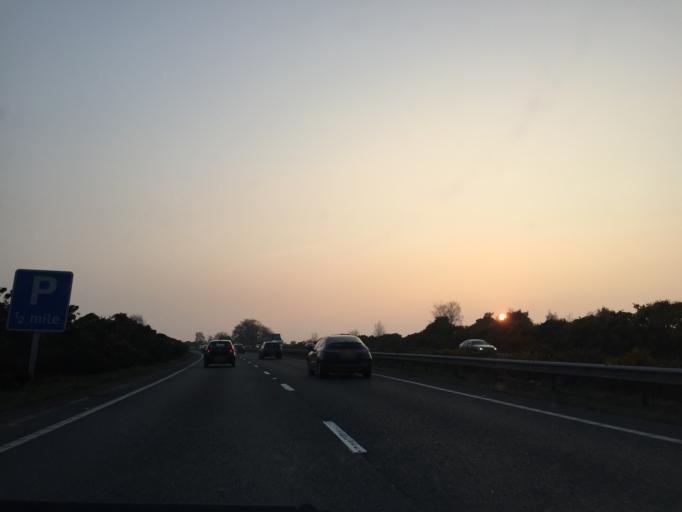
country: GB
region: England
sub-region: Hampshire
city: Cadnam
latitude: 50.8966
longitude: -1.6574
